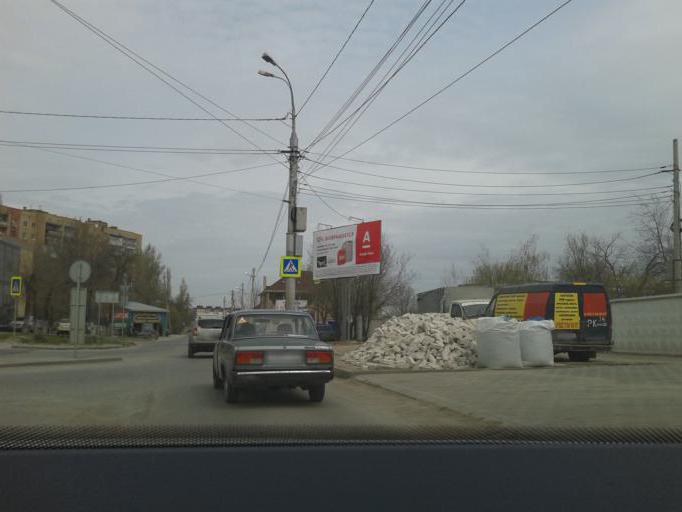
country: RU
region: Volgograd
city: Volgograd
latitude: 48.7409
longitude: 44.5053
